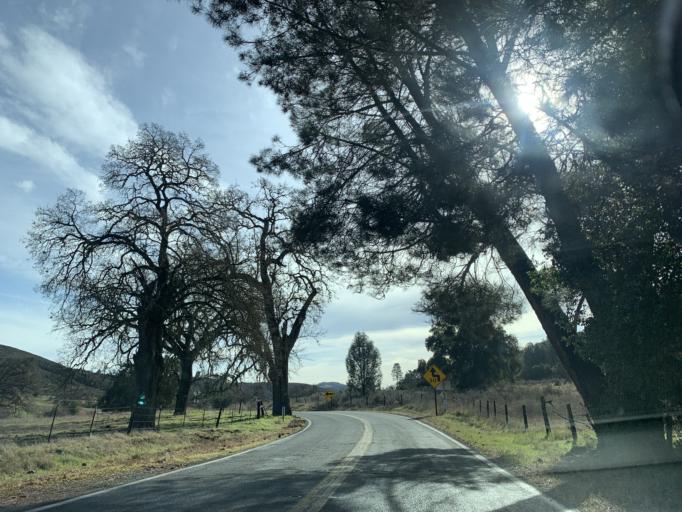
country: US
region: California
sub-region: Monterey County
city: Soledad
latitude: 36.5247
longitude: -121.1417
